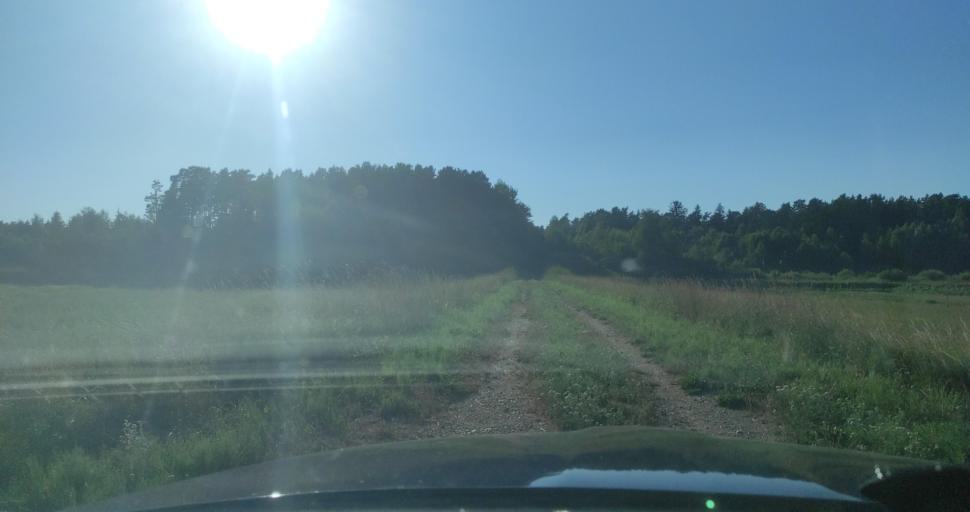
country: LV
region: Skrunda
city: Skrunda
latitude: 56.6783
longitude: 21.9817
